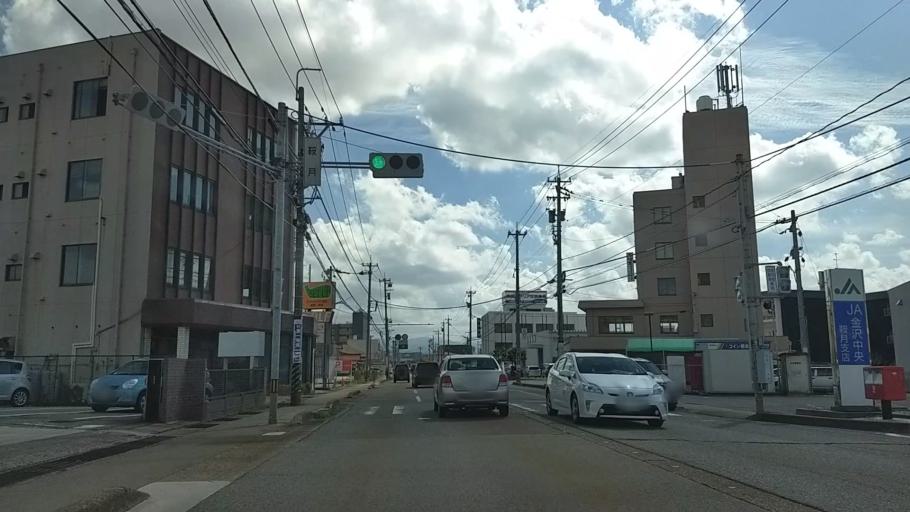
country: JP
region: Ishikawa
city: Kanazawa-shi
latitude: 36.6008
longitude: 136.6369
